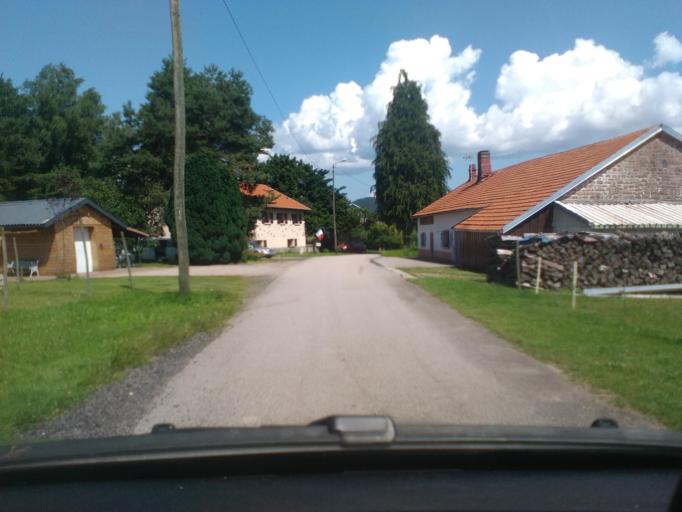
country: FR
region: Lorraine
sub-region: Departement des Vosges
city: Etival-Clairefontaine
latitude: 48.3087
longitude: 6.8033
